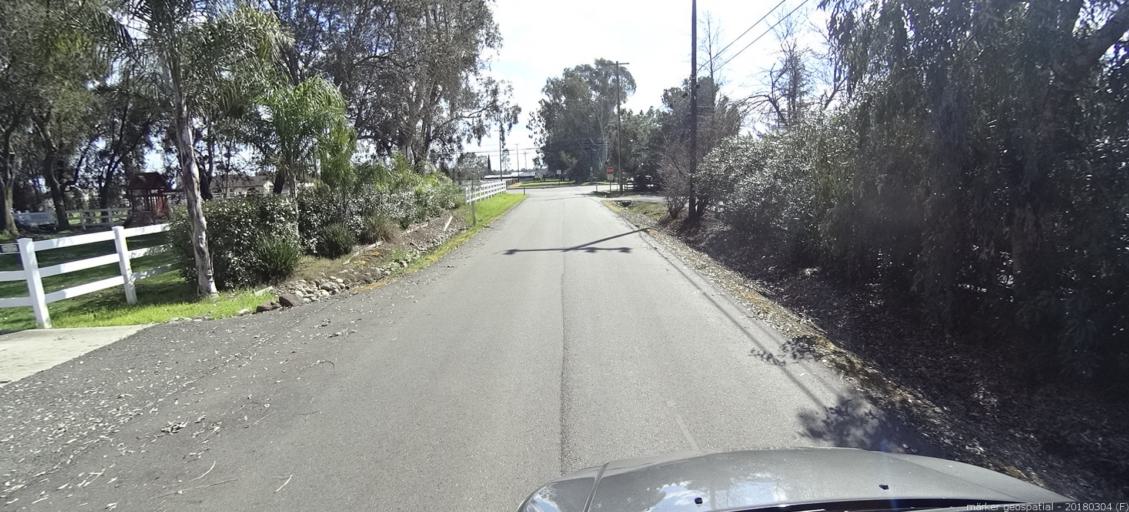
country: US
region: California
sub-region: Sacramento County
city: Vineyard
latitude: 38.4534
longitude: -121.3301
